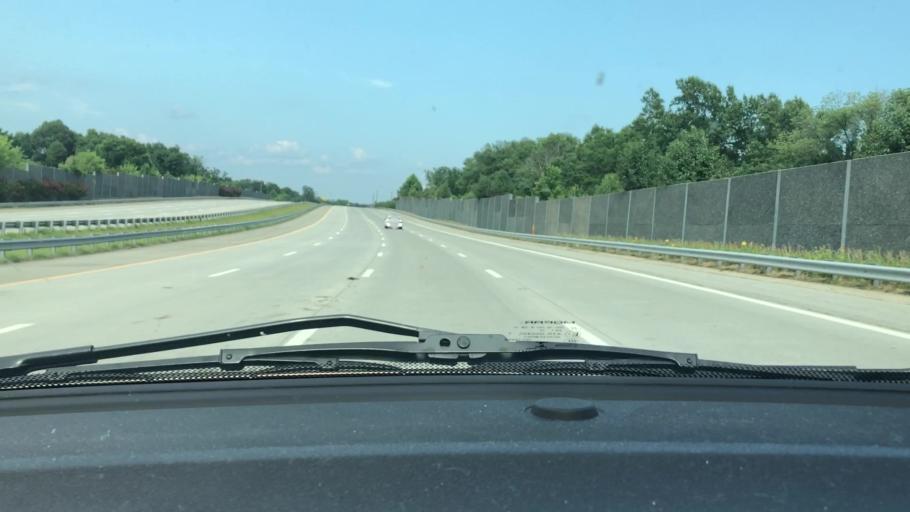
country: US
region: North Carolina
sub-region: Guilford County
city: Jamestown
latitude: 36.0199
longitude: -79.8708
